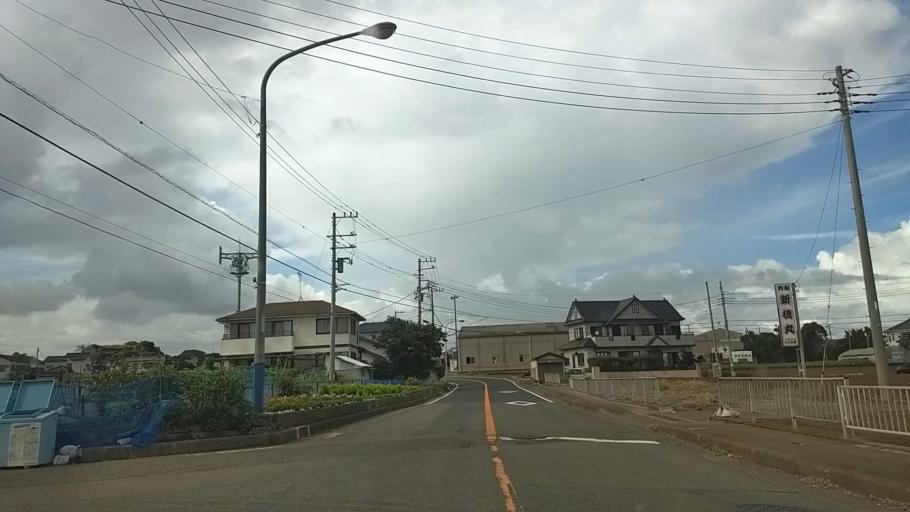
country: JP
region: Kanagawa
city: Miura
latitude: 35.1495
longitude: 139.6686
